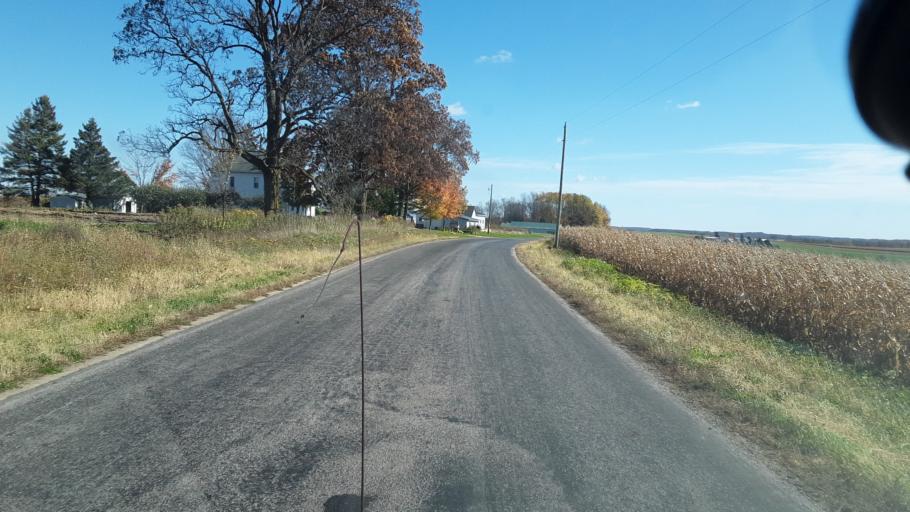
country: US
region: Wisconsin
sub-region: Vernon County
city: Hillsboro
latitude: 43.6921
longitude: -90.4314
